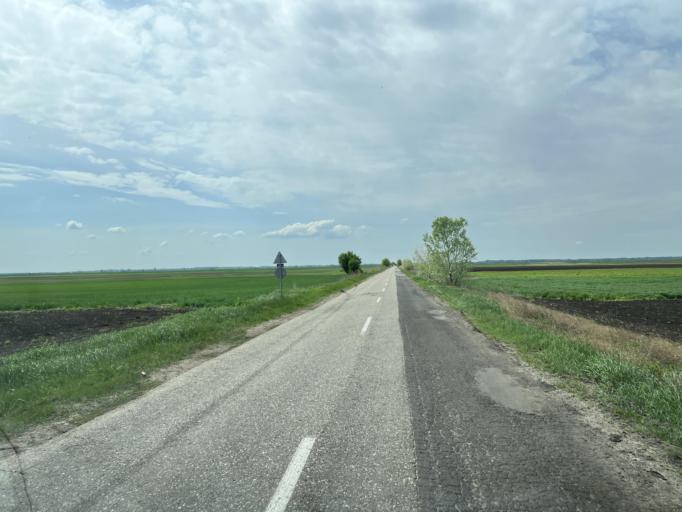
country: HU
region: Pest
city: Tortel
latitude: 47.1544
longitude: 19.9675
